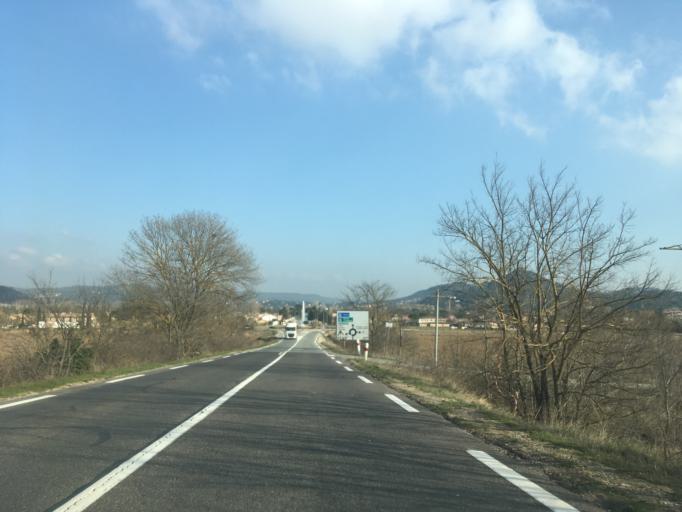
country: FR
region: Provence-Alpes-Cote d'Azur
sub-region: Departement du Var
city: Vidauban
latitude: 43.4120
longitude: 6.4166
